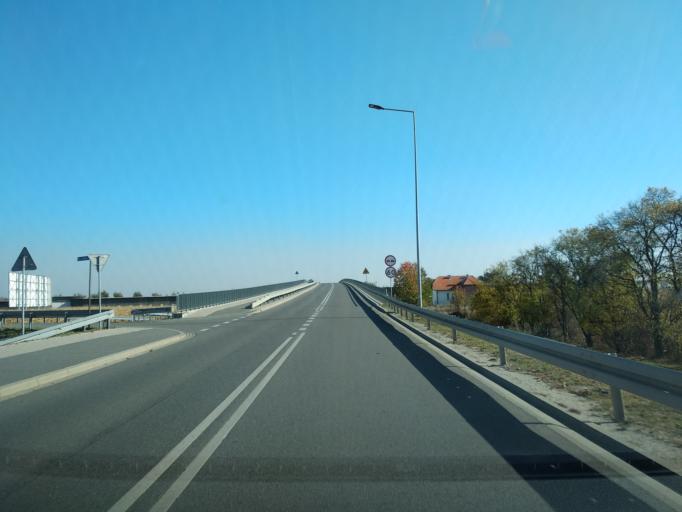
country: PL
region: Lower Silesian Voivodeship
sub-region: Powiat wroclawski
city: Smolec
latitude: 51.0743
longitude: 16.9244
